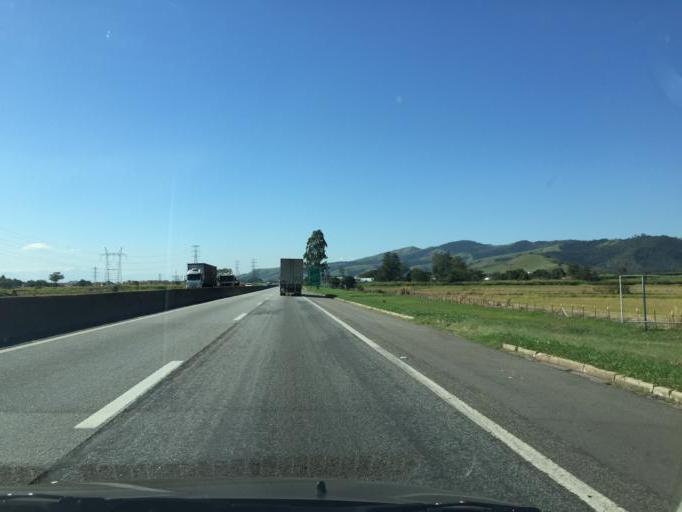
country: BR
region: Sao Paulo
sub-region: Aparecida
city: Aparecida
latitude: -22.9114
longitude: -45.3233
